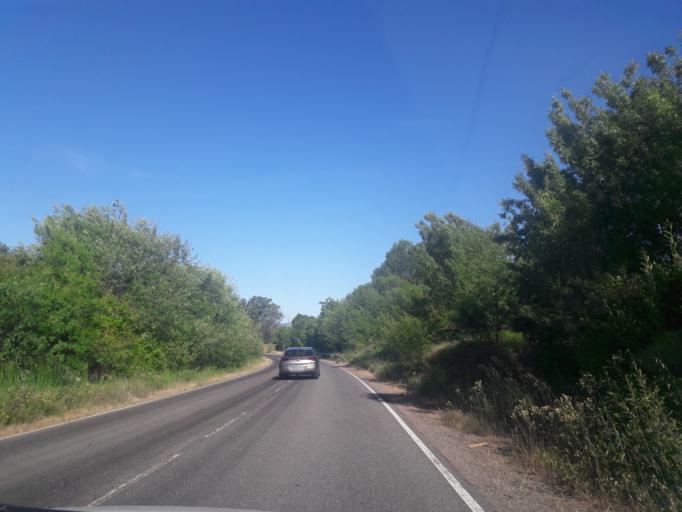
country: ES
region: Castille and Leon
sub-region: Provincia de Salamanca
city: Penacaballera
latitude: 40.3432
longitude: -5.8626
